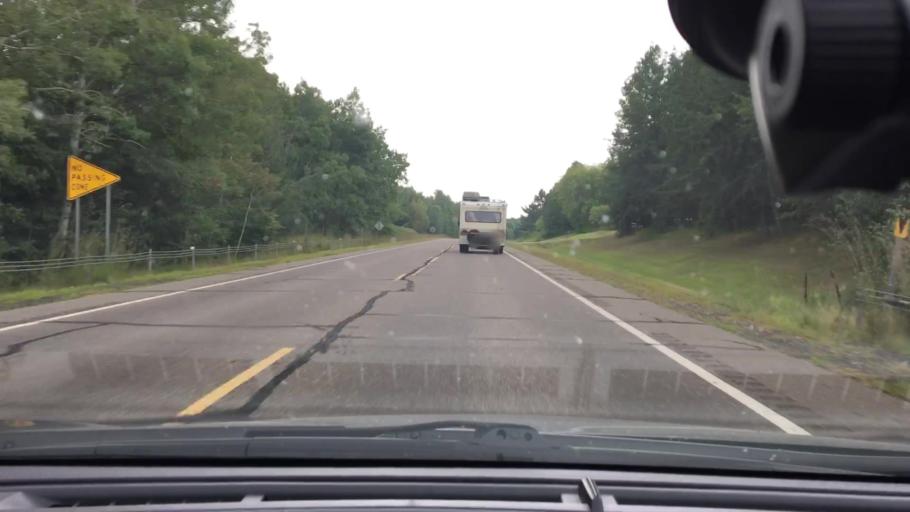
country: US
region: Minnesota
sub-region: Crow Wing County
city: Crosby
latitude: 46.4383
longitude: -93.8754
